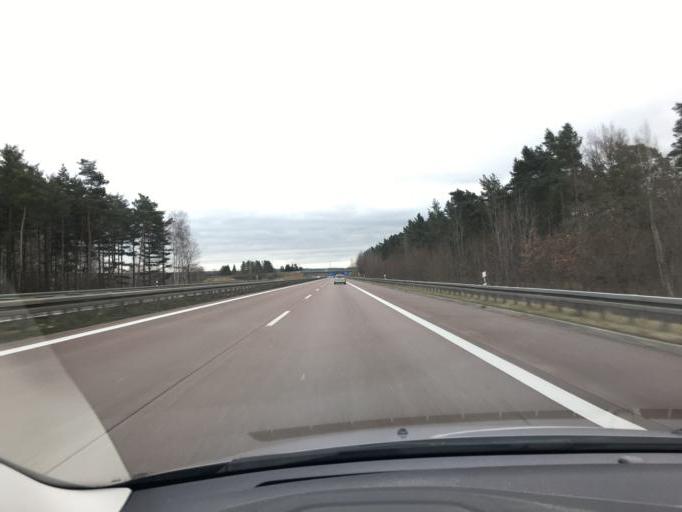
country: DE
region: Saxony
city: Naunhof
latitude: 51.2958
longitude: 12.6195
